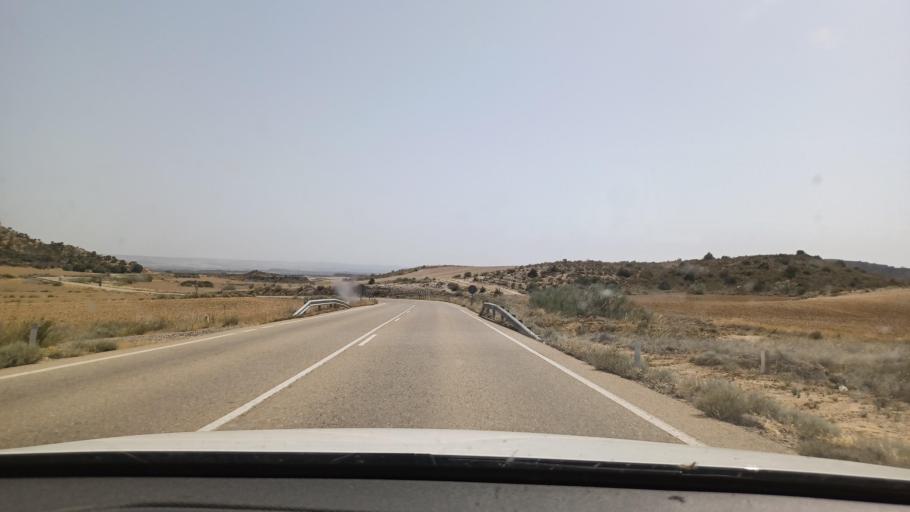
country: ES
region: Aragon
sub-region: Provincia de Zaragoza
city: Chiprana
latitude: 41.3401
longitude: -0.0892
